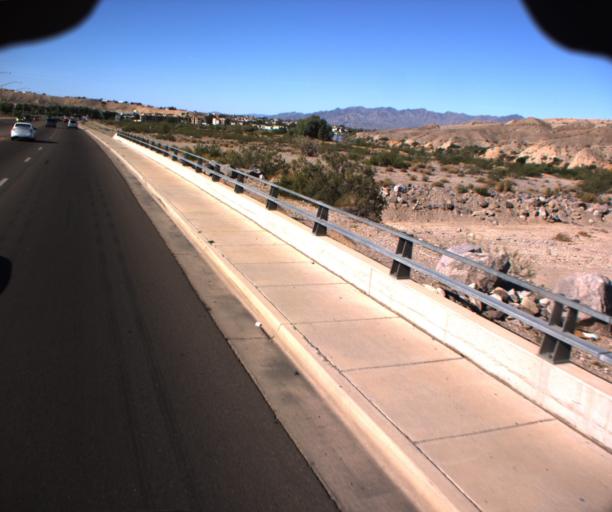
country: US
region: Arizona
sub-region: Mohave County
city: Bullhead City
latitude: 35.1348
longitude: -114.5719
